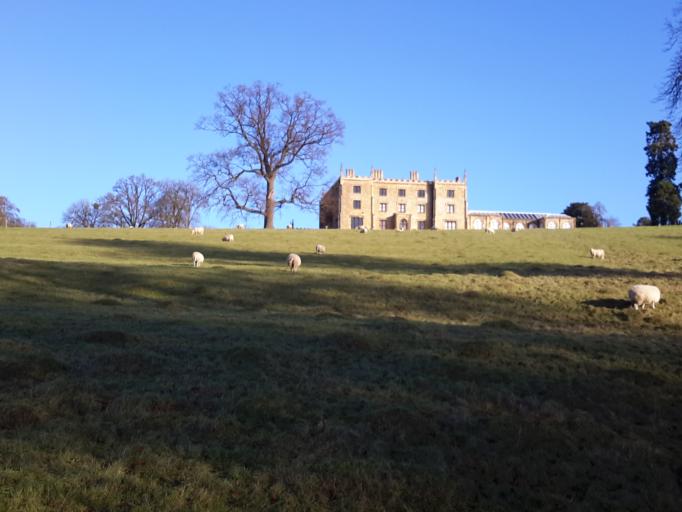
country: GB
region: England
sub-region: Worcestershire
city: Evesham
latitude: 52.1081
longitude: -1.9557
